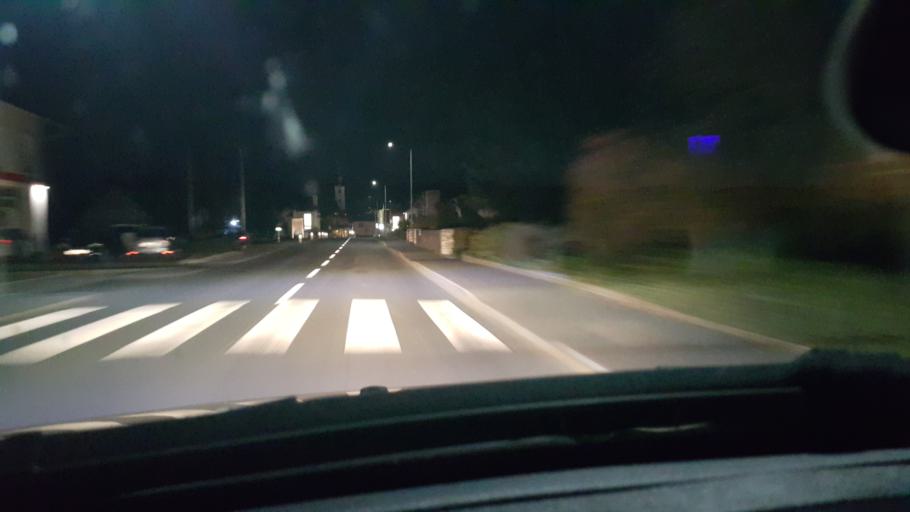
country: AT
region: Styria
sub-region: Politischer Bezirk Deutschlandsberg
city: Sankt Martin im Sulmtal
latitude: 46.7579
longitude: 15.2927
